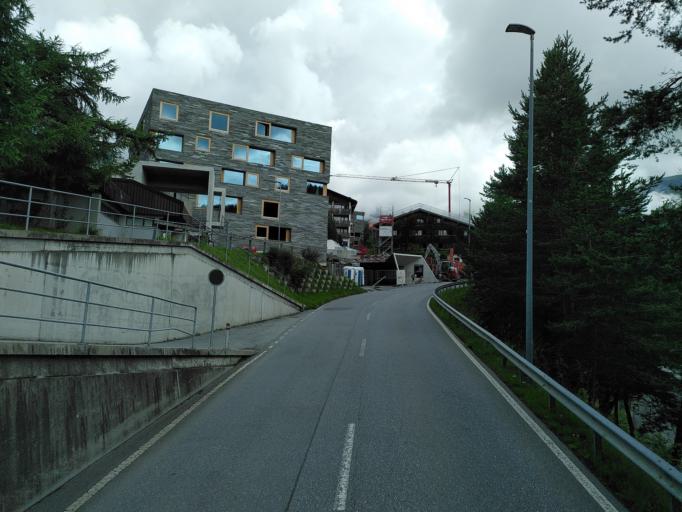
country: CH
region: Grisons
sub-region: Surselva District
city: Laax
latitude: 46.8179
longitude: 9.2654
